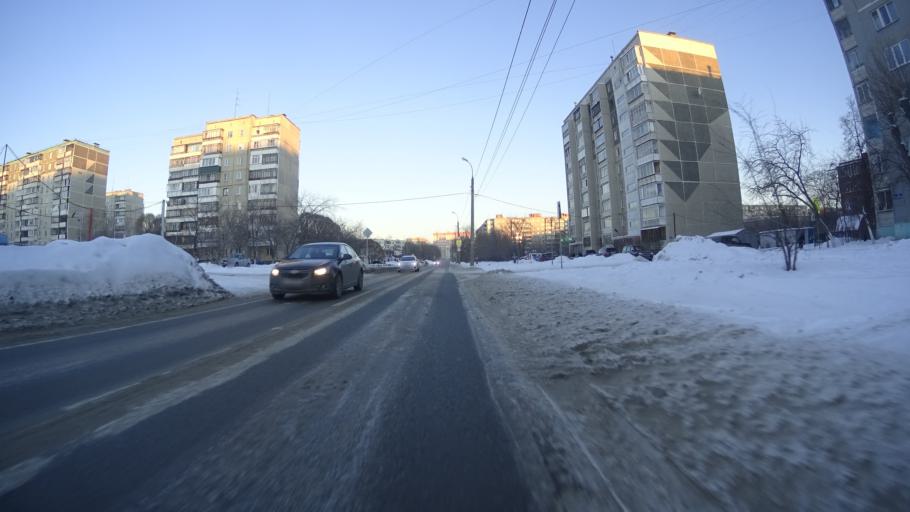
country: RU
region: Chelyabinsk
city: Roshchino
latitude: 55.1988
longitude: 61.3110
